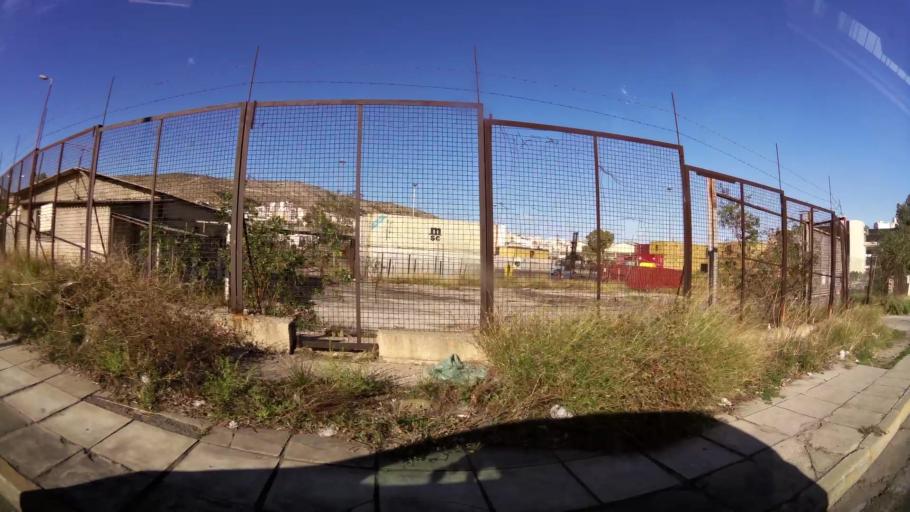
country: GR
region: Attica
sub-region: Nomos Piraios
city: Keratsini
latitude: 37.9624
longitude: 23.6087
